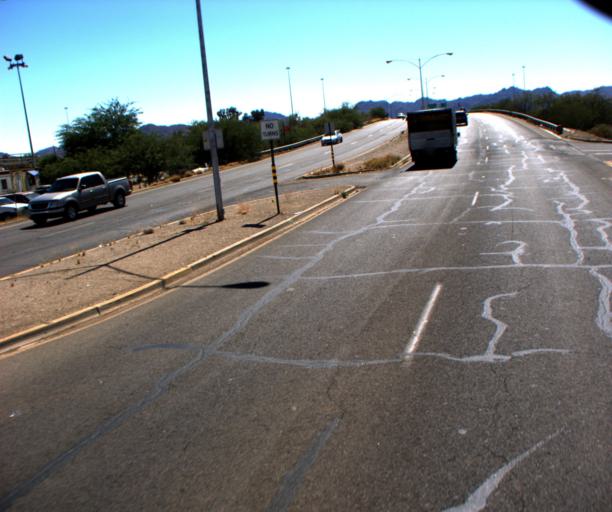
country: US
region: Arizona
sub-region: Pima County
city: Flowing Wells
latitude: 32.2613
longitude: -110.9978
